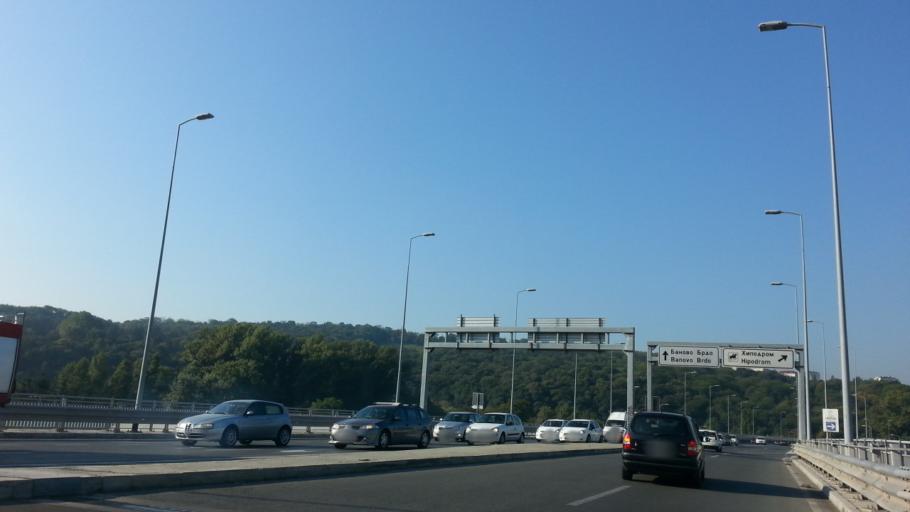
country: RS
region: Central Serbia
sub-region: Belgrade
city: Cukarica
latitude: 44.7856
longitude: 20.4322
